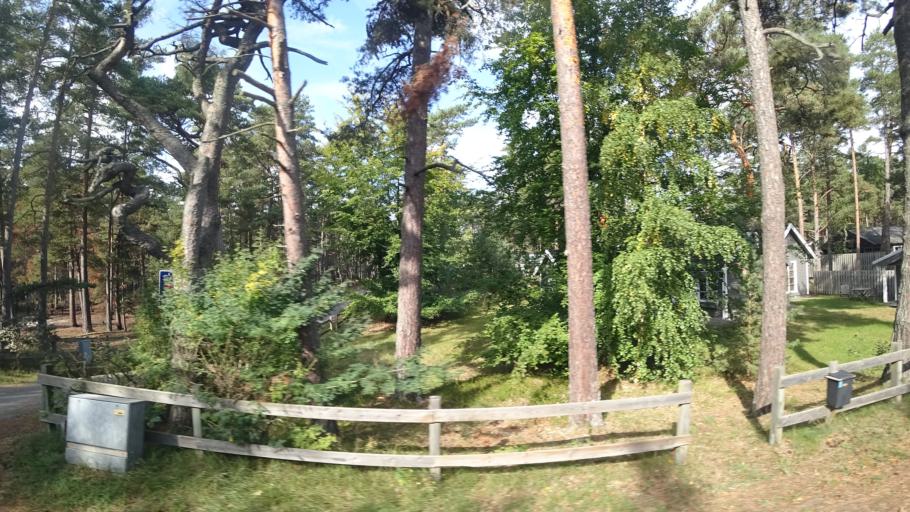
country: SE
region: Skane
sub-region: Kristianstads Kommun
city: Ahus
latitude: 55.9130
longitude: 14.3050
